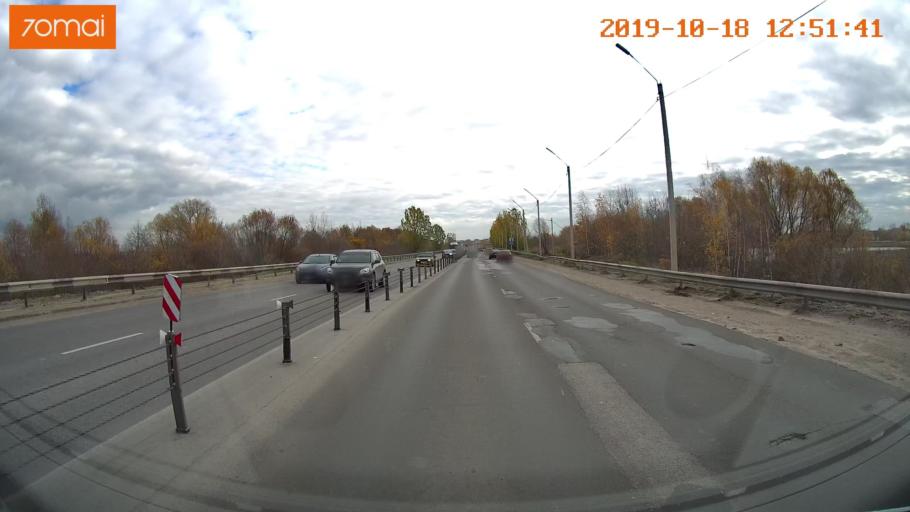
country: RU
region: Rjazan
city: Ryazan'
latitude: 54.6584
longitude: 39.6843
